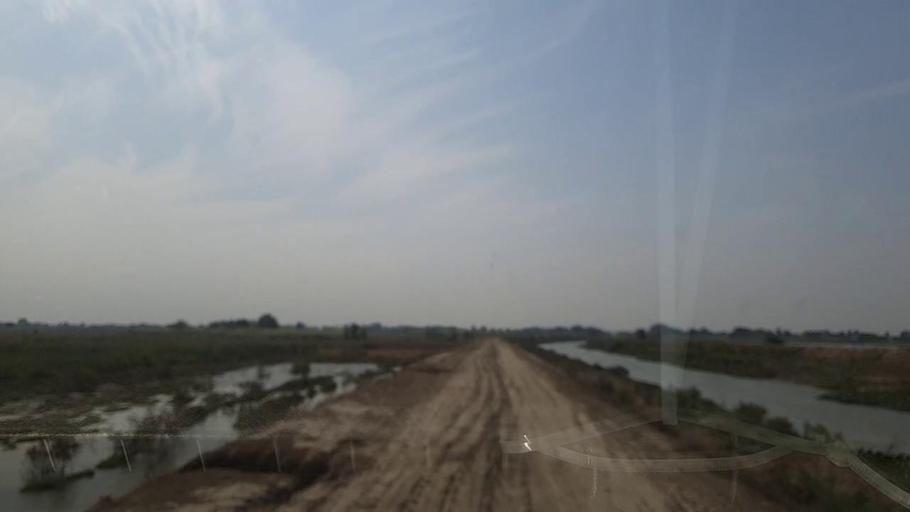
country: PK
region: Sindh
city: Mirpur Batoro
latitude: 24.6454
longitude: 68.2283
